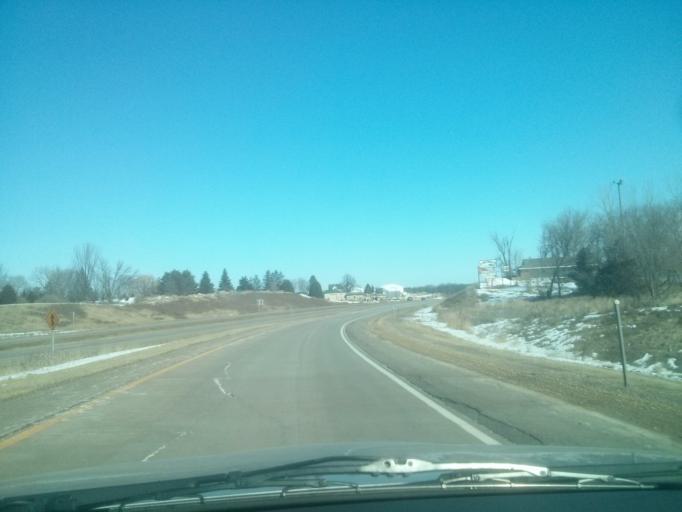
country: US
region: Wisconsin
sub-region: Saint Croix County
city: Somerset
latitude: 45.0905
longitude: -92.7385
